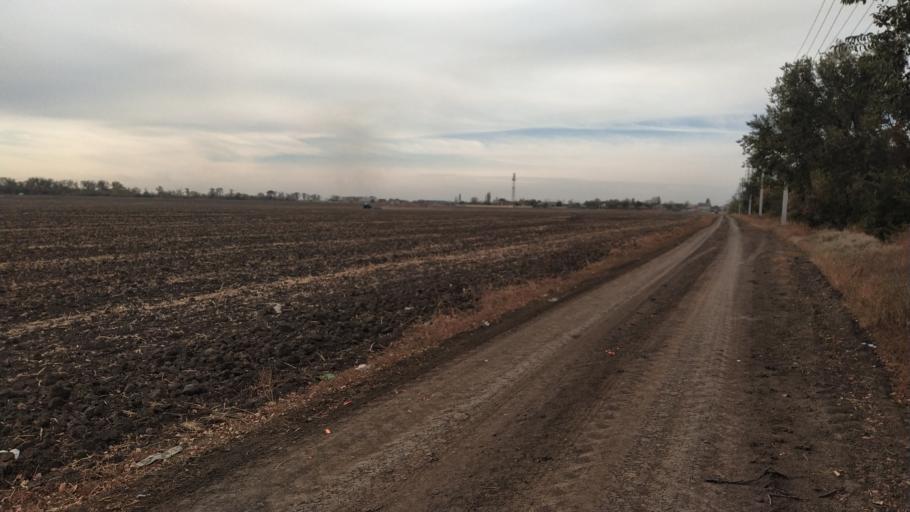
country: RU
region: Rostov
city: Bataysk
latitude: 47.1078
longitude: 39.6859
